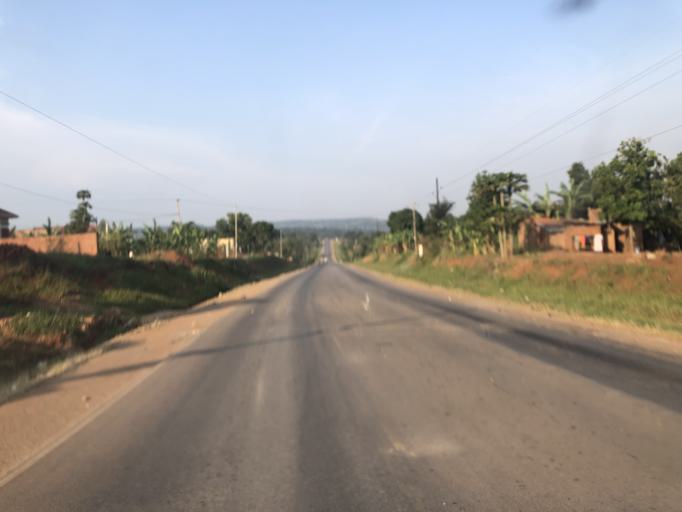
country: UG
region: Central Region
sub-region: Butambala District
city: Gombe
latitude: 0.1189
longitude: 32.1832
